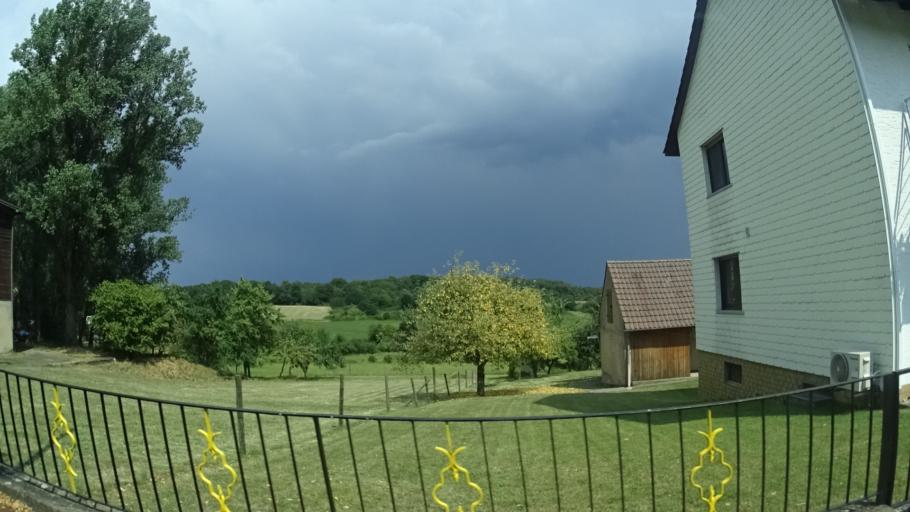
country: DE
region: Hesse
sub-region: Regierungsbezirk Giessen
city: Lauterbach
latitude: 50.5955
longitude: 9.4185
